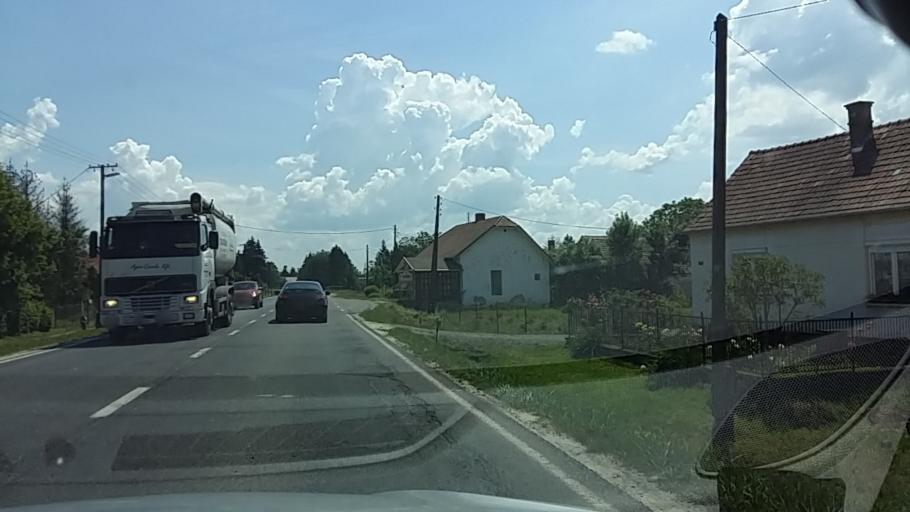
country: AT
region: Burgenland
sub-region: Politischer Bezirk Gussing
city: Heiligenbrunn
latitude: 46.9701
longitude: 16.4018
